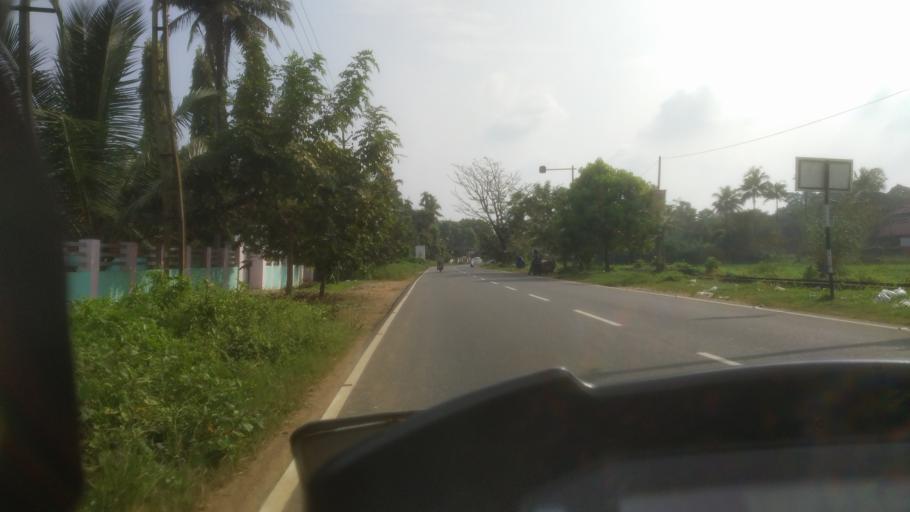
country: IN
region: Kerala
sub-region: Ernakulam
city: Angamali
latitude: 10.1636
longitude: 76.4008
